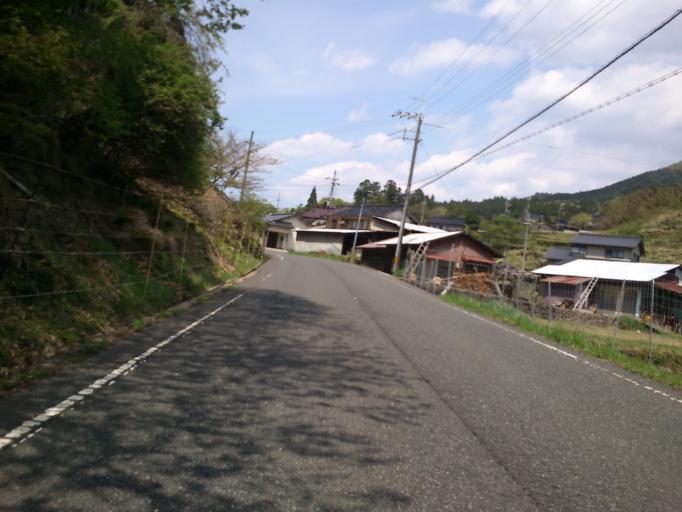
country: JP
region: Hyogo
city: Toyooka
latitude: 35.3965
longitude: 134.9454
